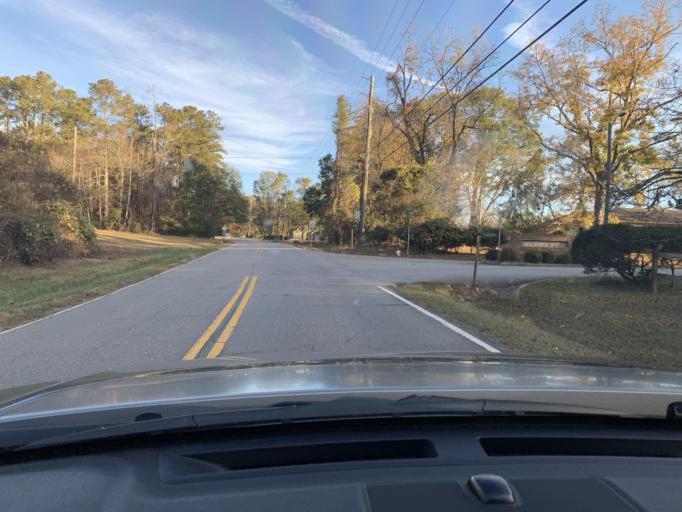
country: US
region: Georgia
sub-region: Clarke County
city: Country Club Estates
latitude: 33.9295
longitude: -83.4588
